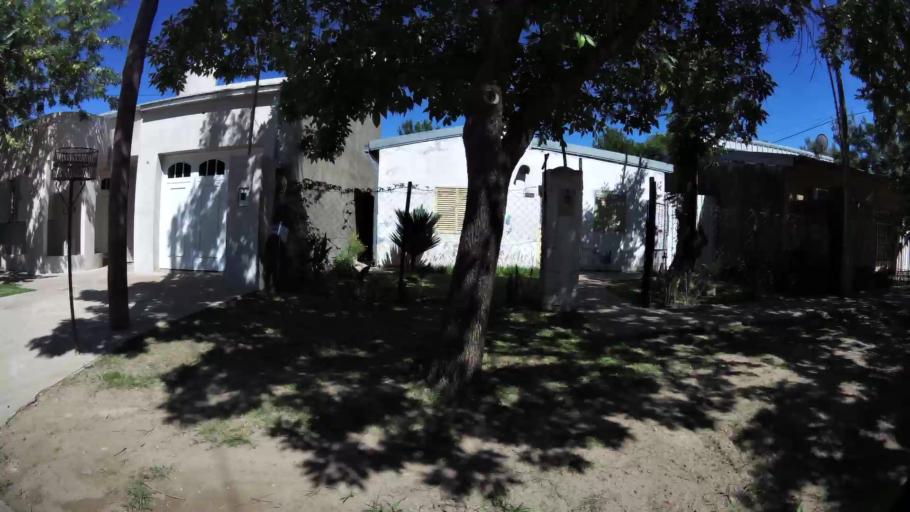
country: AR
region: Santa Fe
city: Esperanza
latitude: -31.4325
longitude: -60.9243
